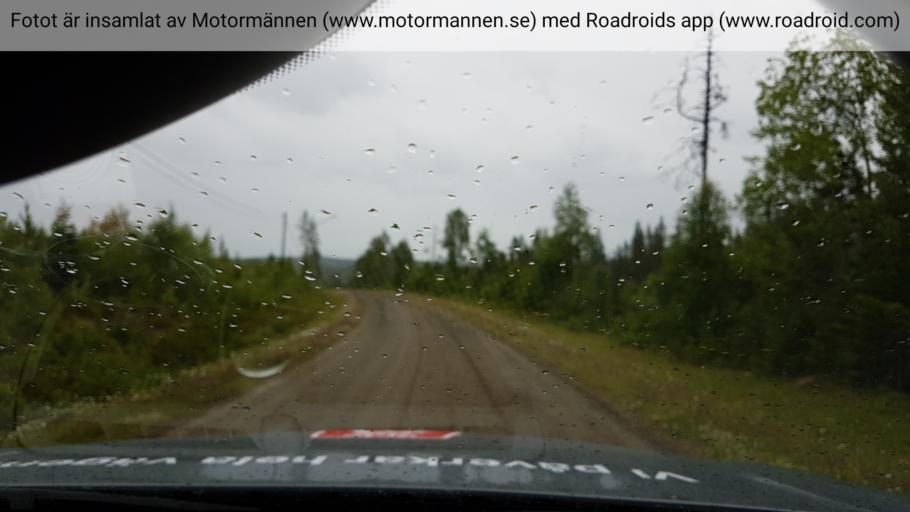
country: SE
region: Jaemtland
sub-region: Bergs Kommun
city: Hoverberg
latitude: 62.5663
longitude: 14.6721
